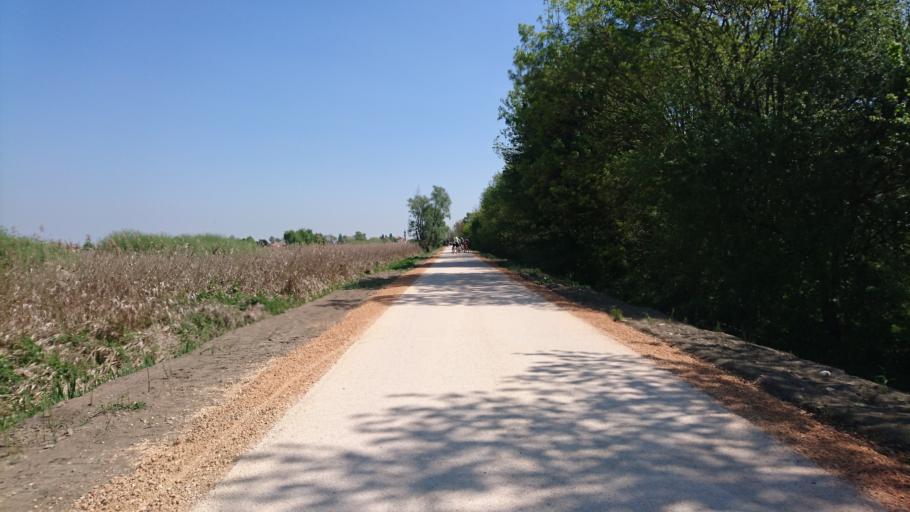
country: IT
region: Veneto
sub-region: Provincia di Venezia
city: Musile di Piave
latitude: 45.5754
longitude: 12.5363
